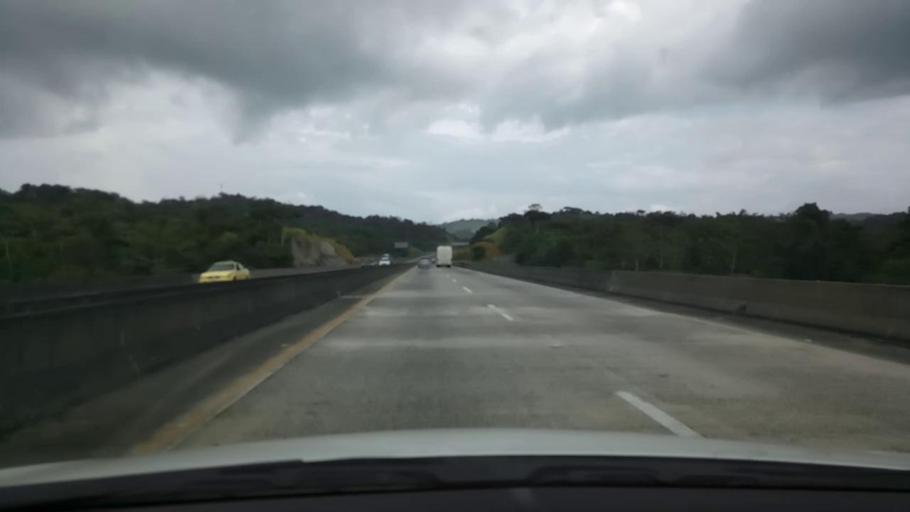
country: PA
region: Colon
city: Gatun
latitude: 9.2825
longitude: -79.7718
